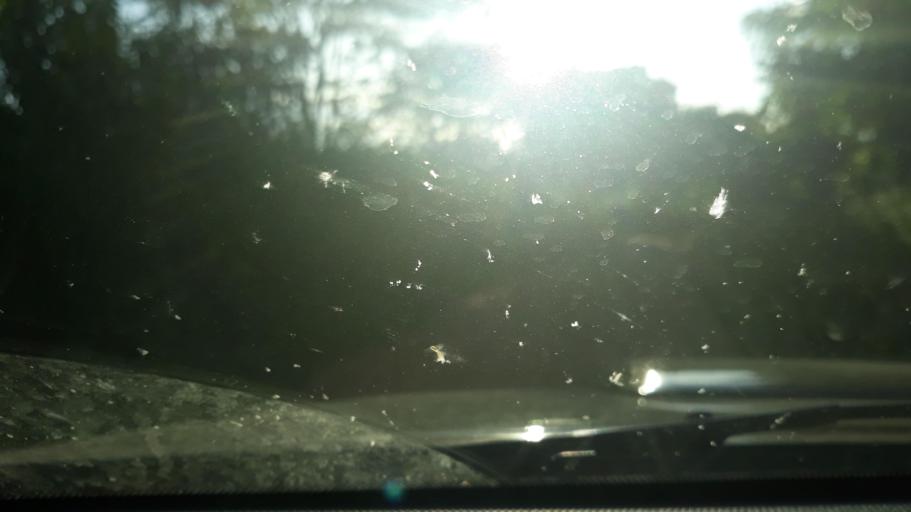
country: BR
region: Bahia
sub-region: Riacho De Santana
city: Riacho de Santana
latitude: -13.8475
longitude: -42.7476
